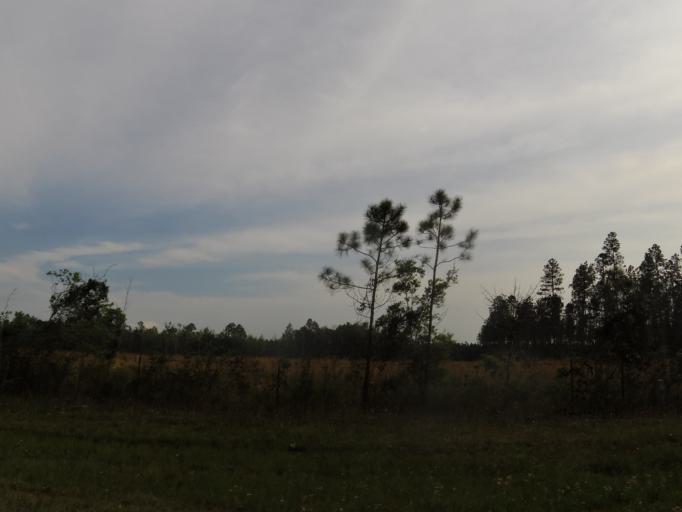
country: US
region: Florida
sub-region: Nassau County
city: Hilliard
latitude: 30.6972
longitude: -81.7913
